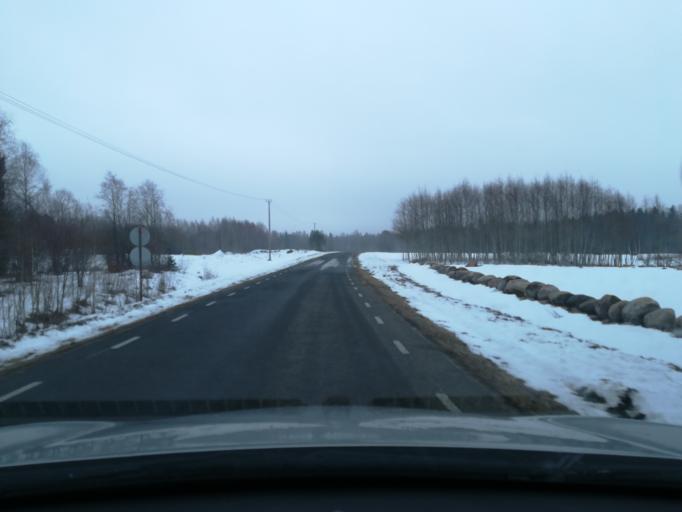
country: EE
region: Harju
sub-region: Loksa linn
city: Loksa
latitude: 59.4727
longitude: 25.6909
